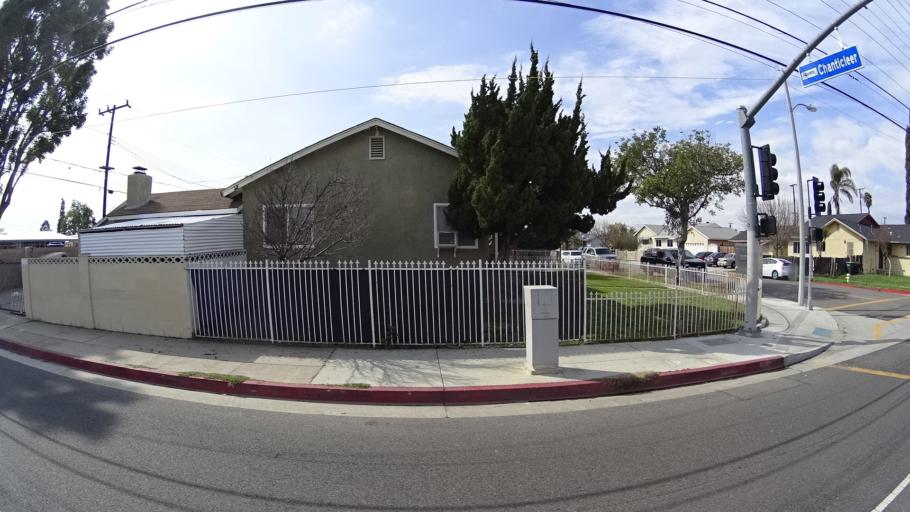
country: US
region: California
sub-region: Orange County
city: Stanton
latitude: 33.8123
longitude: -117.9846
